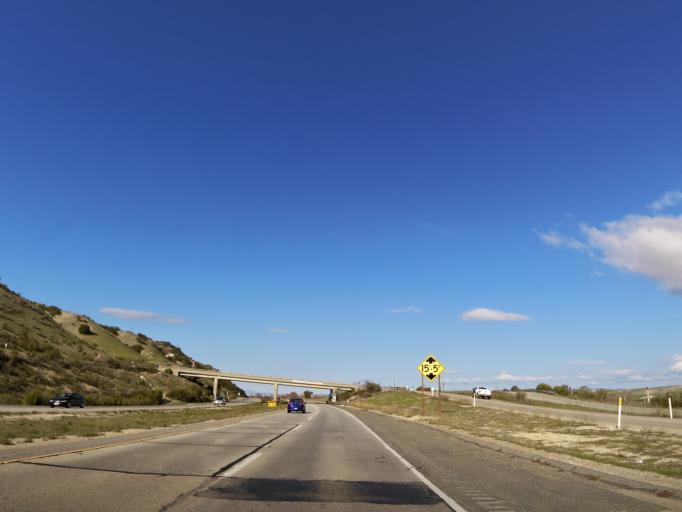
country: US
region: California
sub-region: San Luis Obispo County
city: Lake Nacimiento
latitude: 35.9456
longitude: -120.8753
